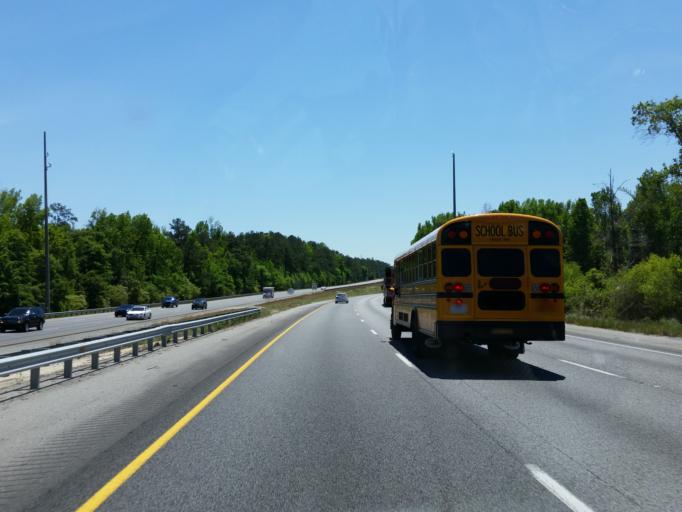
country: US
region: Georgia
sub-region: Bibb County
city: West Point
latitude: 32.8005
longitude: -83.7215
